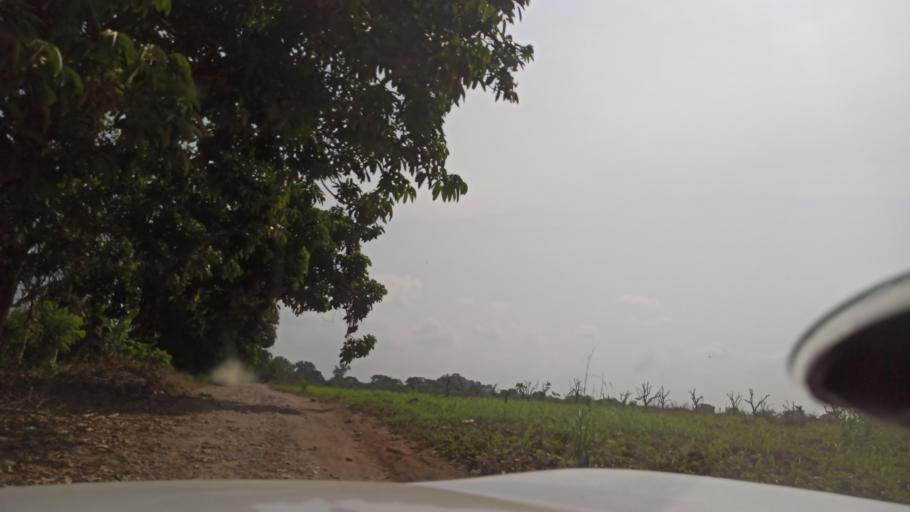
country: MX
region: Veracruz
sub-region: Martinez de la Torre
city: El Progreso
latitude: 20.1466
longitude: -97.0629
